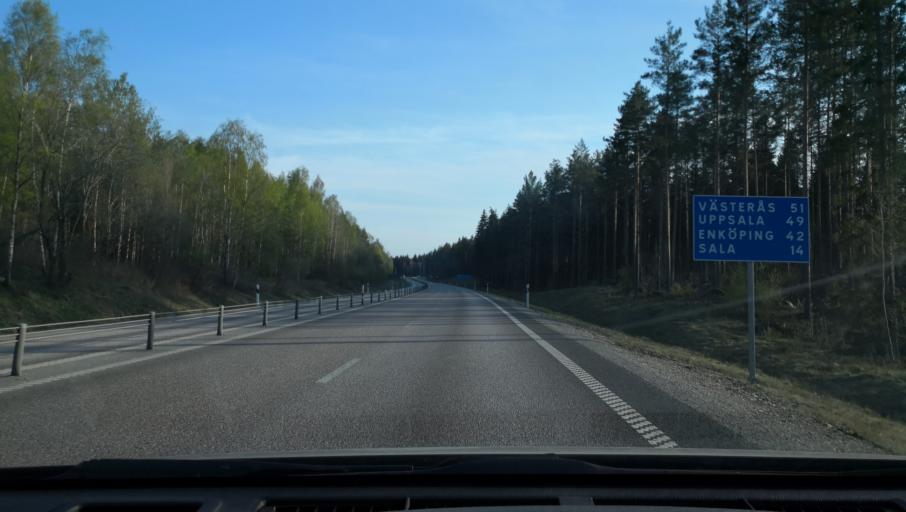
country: SE
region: Uppsala
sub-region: Heby Kommun
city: Heby
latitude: 59.9434
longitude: 16.8301
